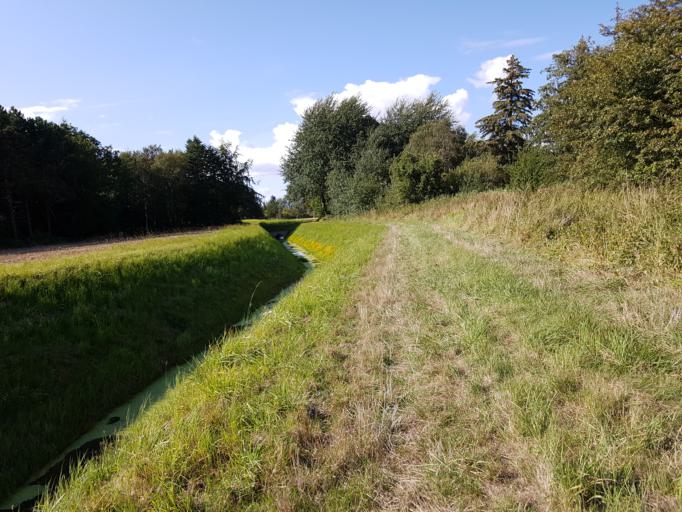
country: DK
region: Zealand
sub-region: Guldborgsund Kommune
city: Nykobing Falster
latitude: 54.6014
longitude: 11.9483
